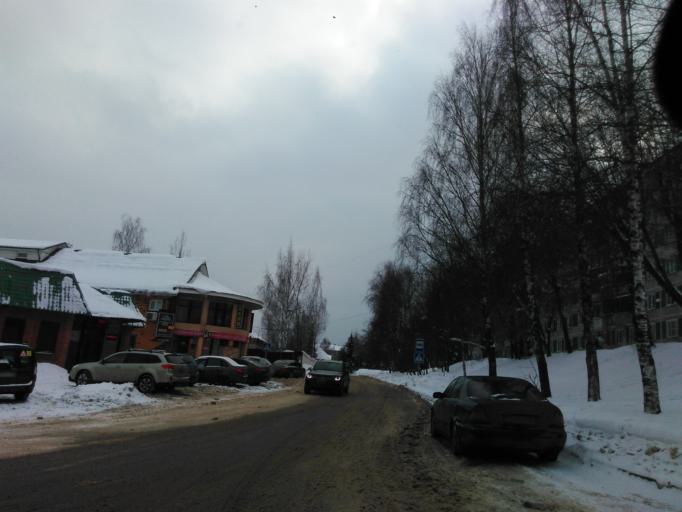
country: RU
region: Moskovskaya
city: Yakhroma
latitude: 56.2819
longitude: 37.4848
